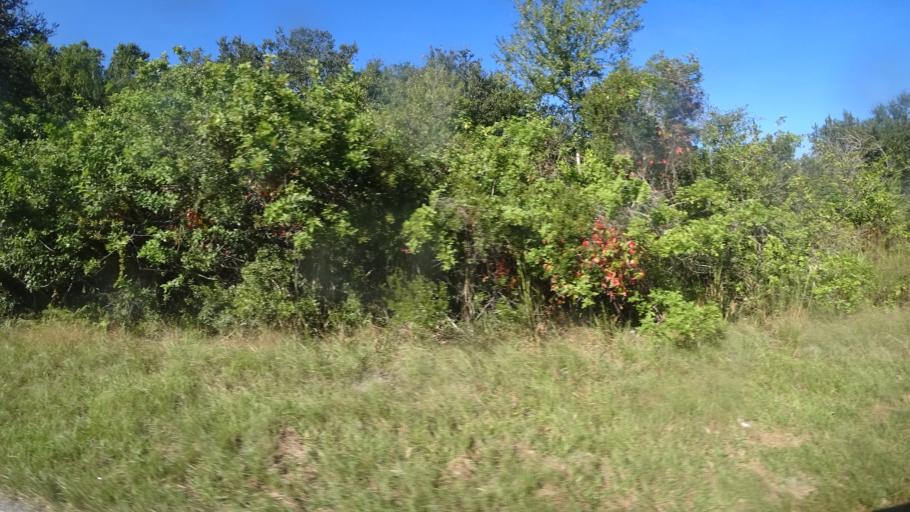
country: US
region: Florida
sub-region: Hillsborough County
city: Wimauma
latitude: 27.6326
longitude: -82.2925
